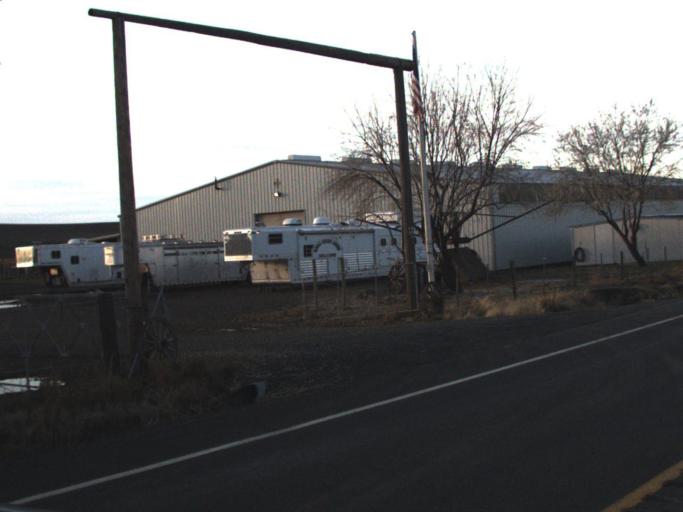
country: US
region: Washington
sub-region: Garfield County
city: Pomeroy
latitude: 46.7914
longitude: -117.6874
